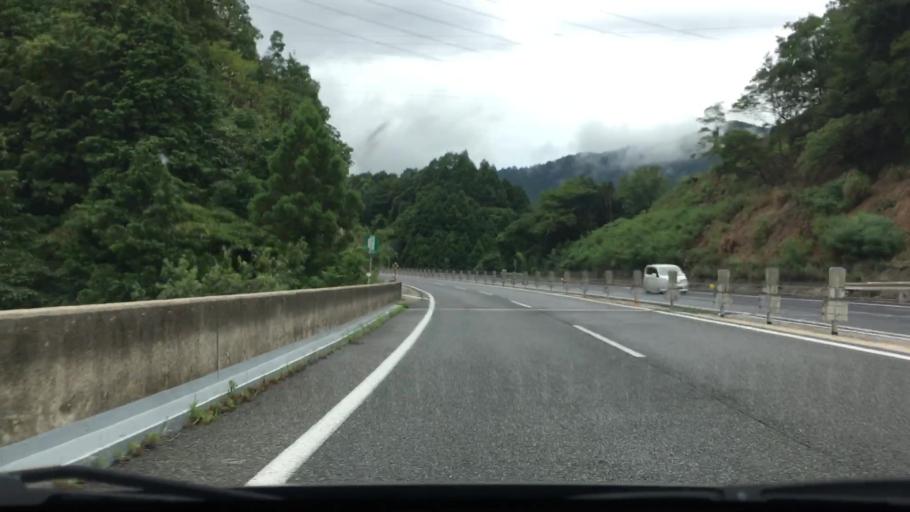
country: JP
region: Hiroshima
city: Hiroshima-shi
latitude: 34.5592
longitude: 132.4505
